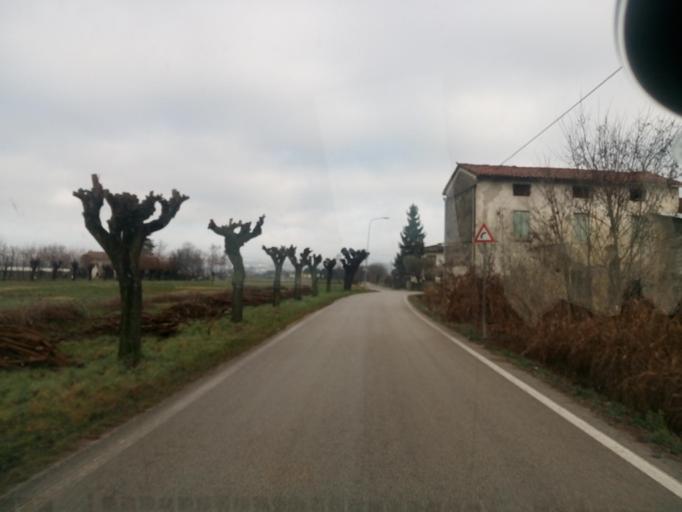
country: IT
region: Veneto
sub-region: Provincia di Vicenza
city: Sandrigo
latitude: 45.6709
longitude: 11.5808
